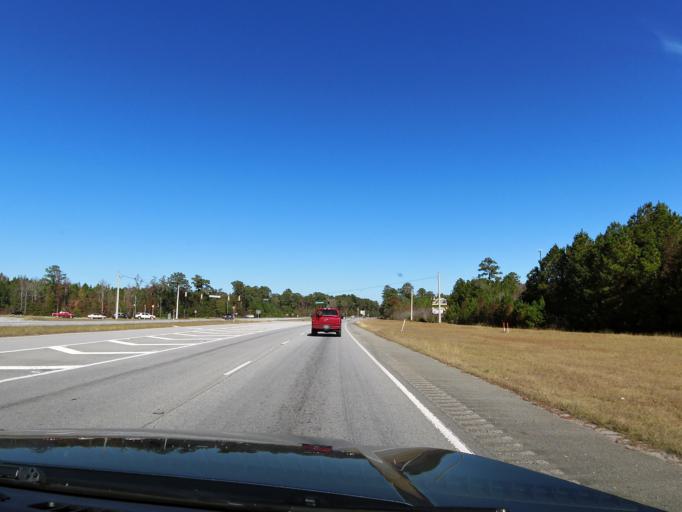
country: US
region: Georgia
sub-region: Liberty County
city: Midway
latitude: 31.8776
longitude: -81.3954
